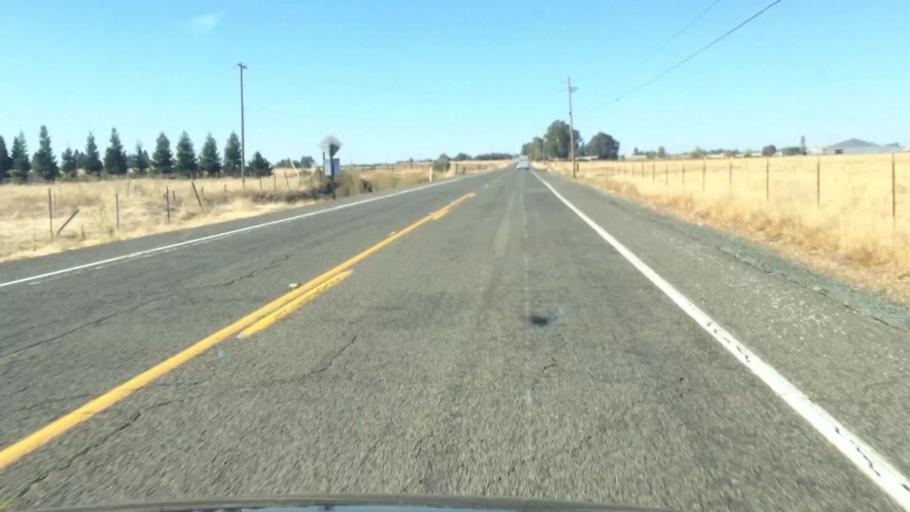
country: US
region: California
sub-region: Sacramento County
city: Clay
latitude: 38.3958
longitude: -121.1691
